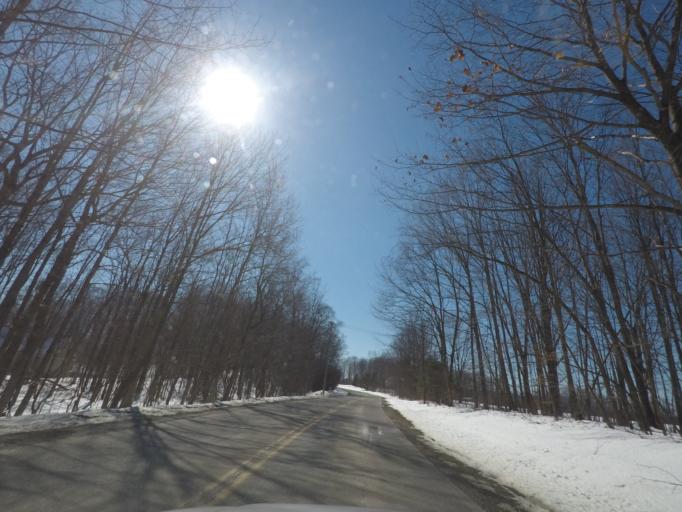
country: US
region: New York
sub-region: Saratoga County
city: Stillwater
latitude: 43.0272
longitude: -73.6697
